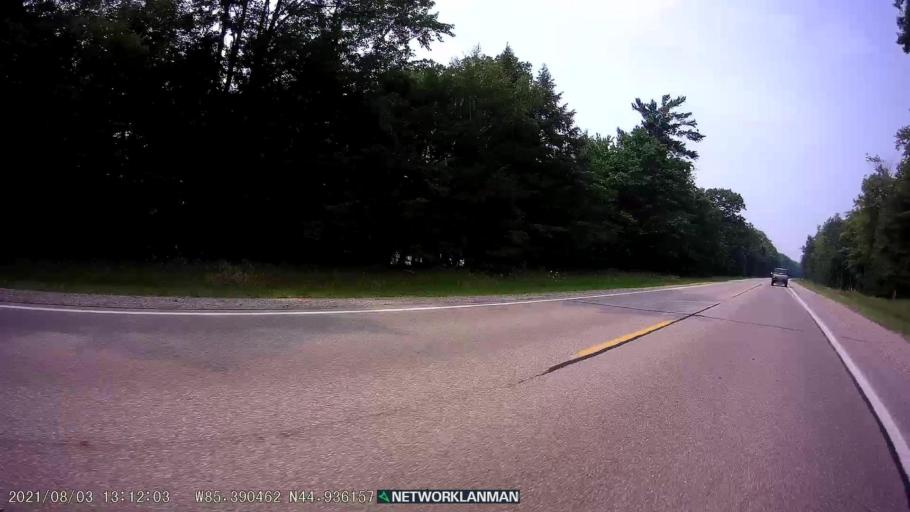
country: US
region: Michigan
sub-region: Antrim County
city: Elk Rapids
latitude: 44.9362
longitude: -85.3903
